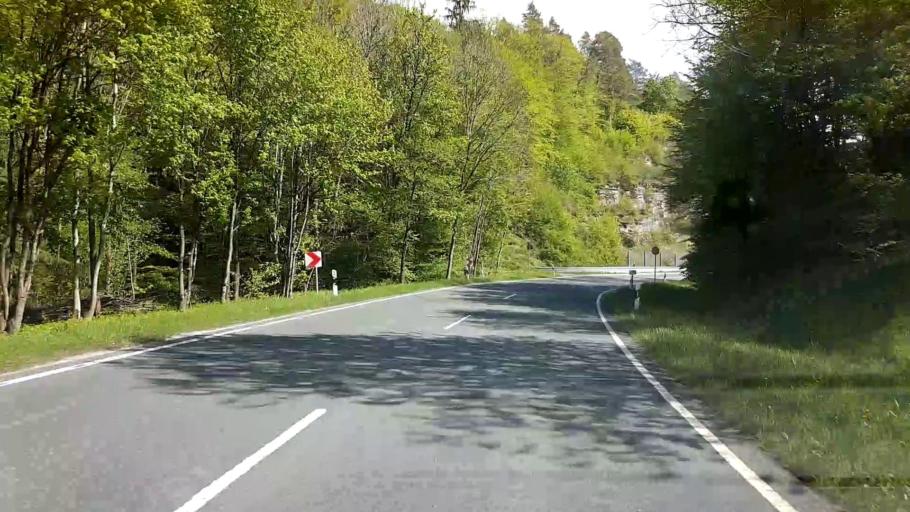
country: DE
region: Bavaria
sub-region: Upper Franconia
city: Unterleinleiter
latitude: 49.8115
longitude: 11.1447
